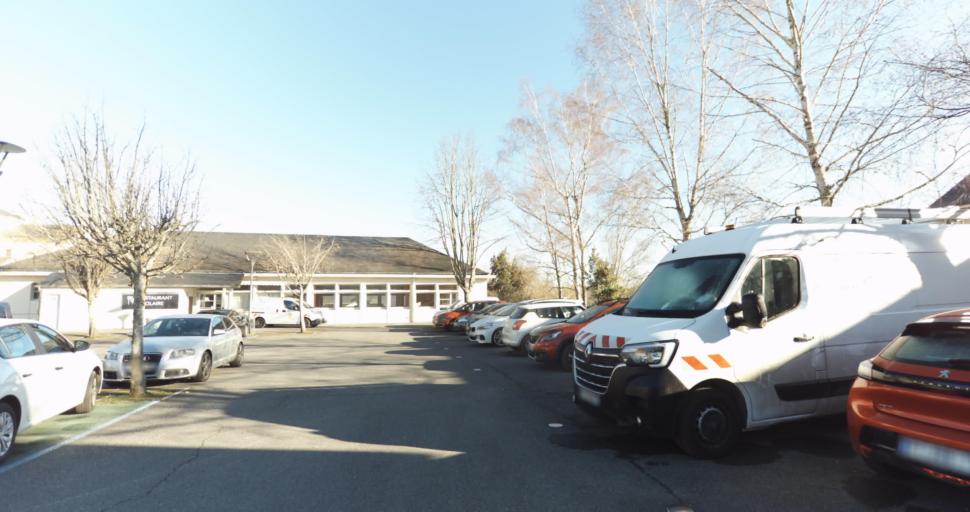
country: FR
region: Aquitaine
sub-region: Departement des Pyrenees-Atlantiques
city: Morlaas
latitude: 43.3443
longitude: -0.2624
